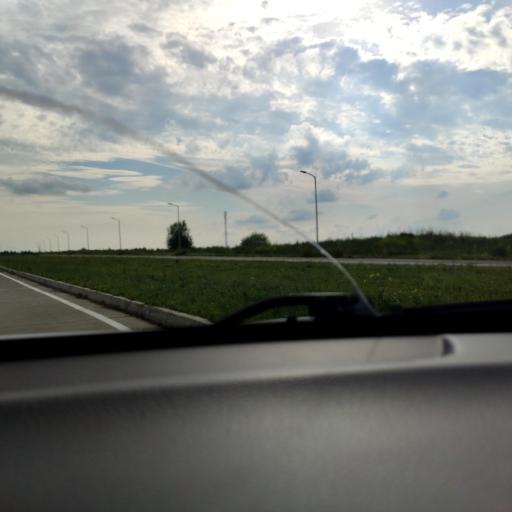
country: RU
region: Tatarstan
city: Sviyazhsk
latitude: 55.7466
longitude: 48.7383
